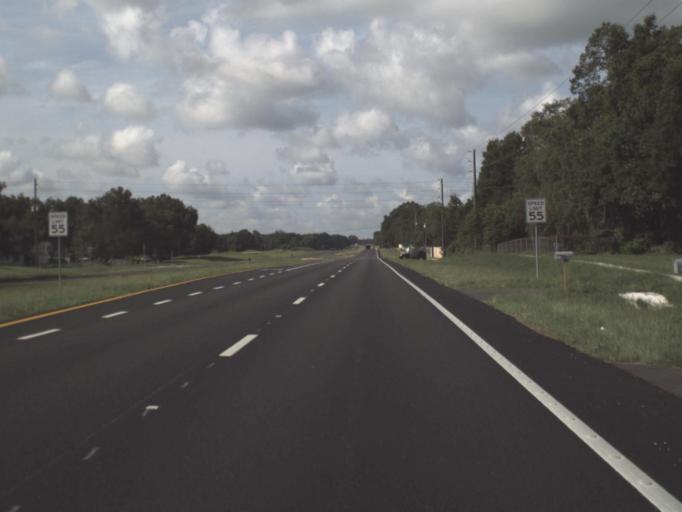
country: US
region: Florida
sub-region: Pasco County
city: Lacoochee
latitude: 28.4510
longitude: -82.1872
